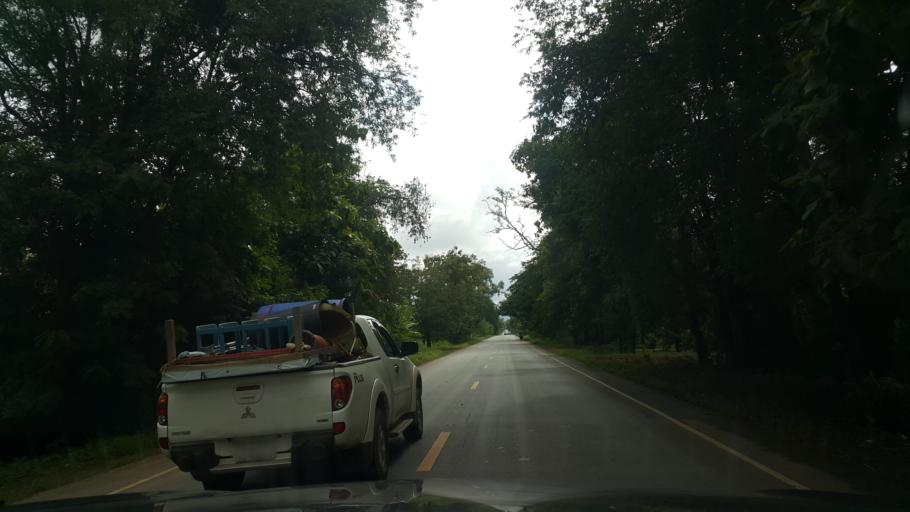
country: TH
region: Sukhothai
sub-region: Amphoe Si Satchanalai
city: Si Satchanalai
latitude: 17.5437
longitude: 99.8307
